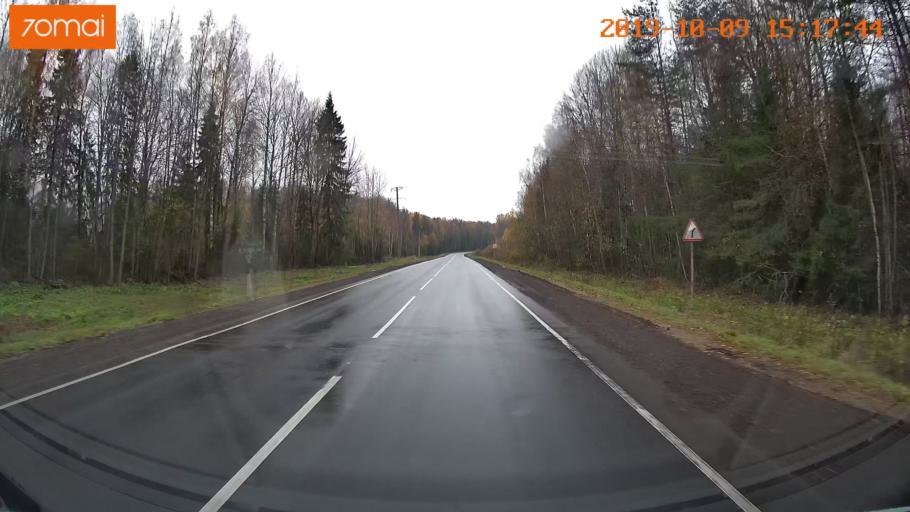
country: RU
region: Kostroma
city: Susanino
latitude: 58.0943
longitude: 41.5817
